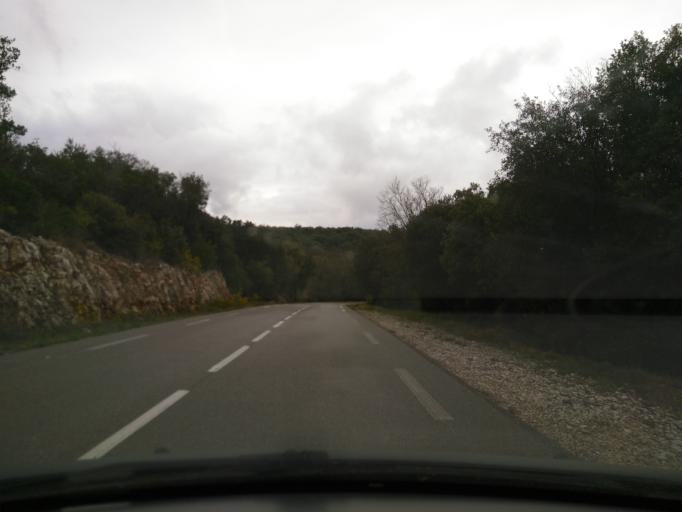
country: FR
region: Languedoc-Roussillon
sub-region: Departement du Gard
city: Barjac
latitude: 44.3320
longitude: 4.4121
